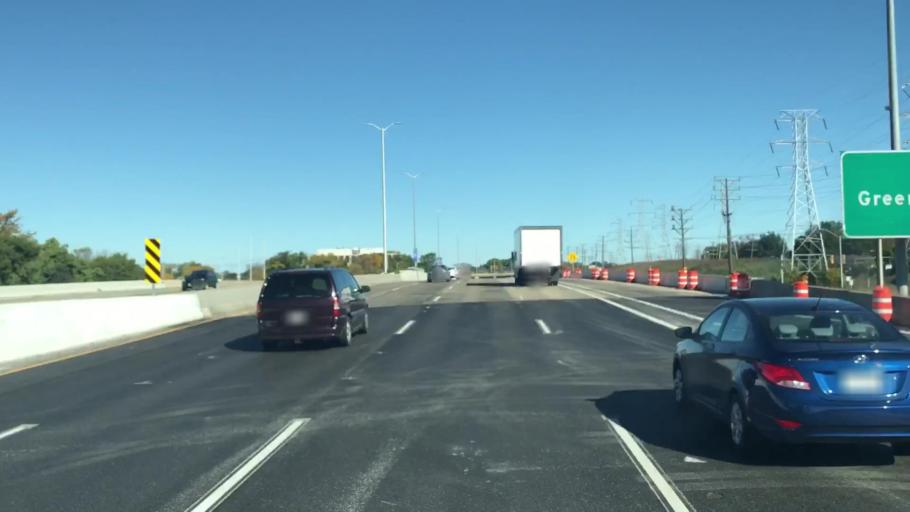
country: US
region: Wisconsin
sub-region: Milwaukee County
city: West Allis
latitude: 42.9983
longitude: -88.0379
